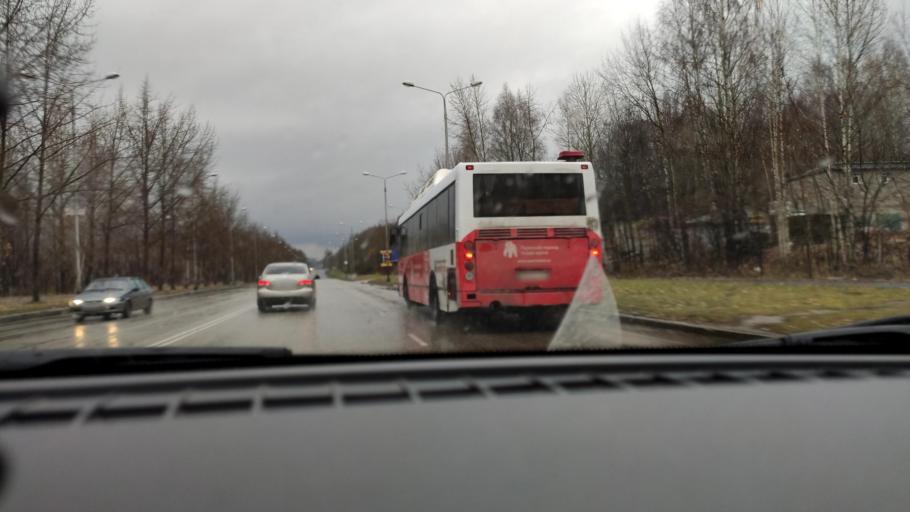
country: RU
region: Perm
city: Perm
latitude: 58.1022
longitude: 56.3909
